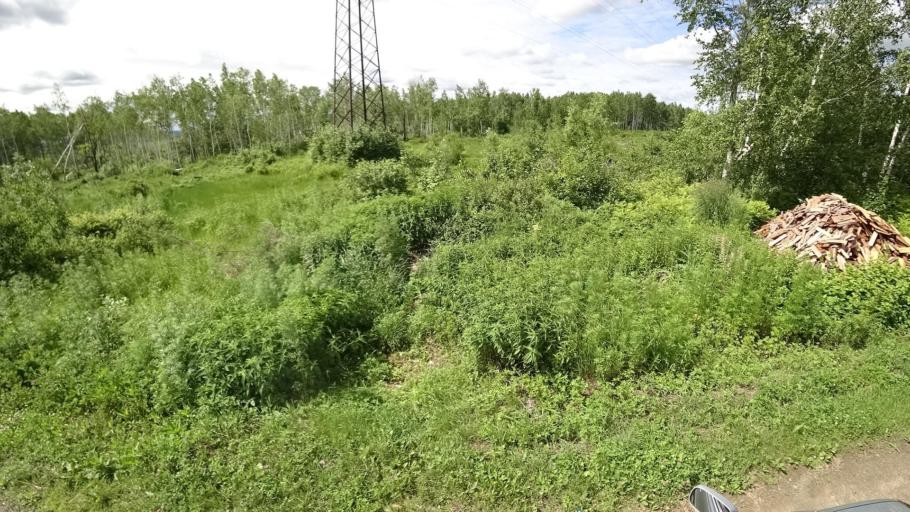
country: RU
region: Khabarovsk Krai
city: Litovko
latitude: 49.3683
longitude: 135.1659
